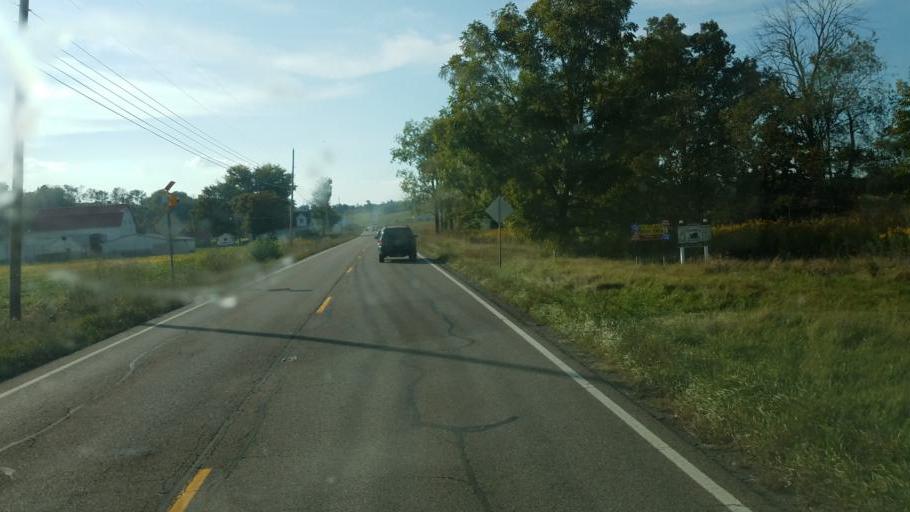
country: US
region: Ohio
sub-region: Knox County
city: Gambier
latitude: 40.4108
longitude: -82.3732
